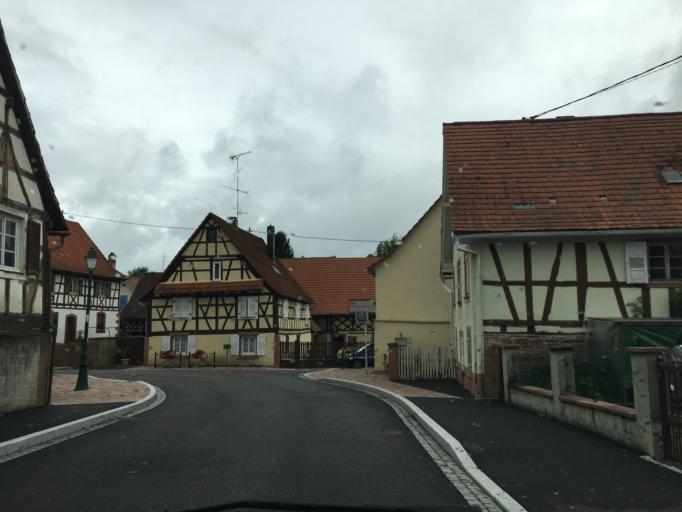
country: FR
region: Alsace
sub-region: Departement du Bas-Rhin
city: Lembach
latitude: 49.0024
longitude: 7.7933
